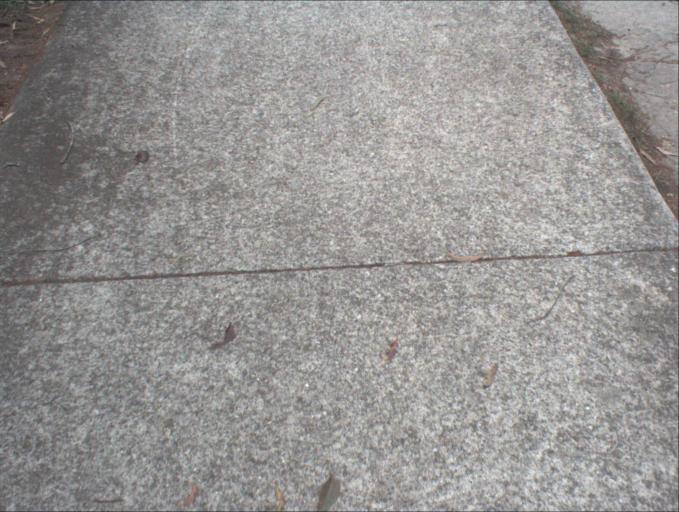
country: AU
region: Queensland
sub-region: Logan
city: Logan Reserve
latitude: -27.6912
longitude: 153.0783
